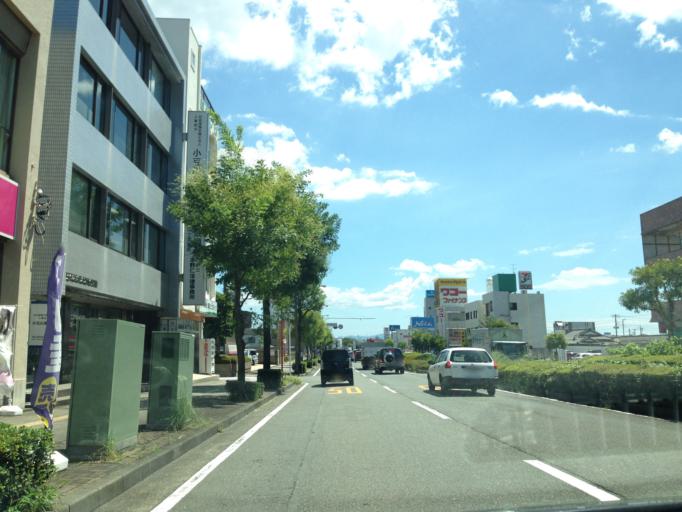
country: JP
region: Shizuoka
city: Fuji
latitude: 35.1603
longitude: 138.6800
